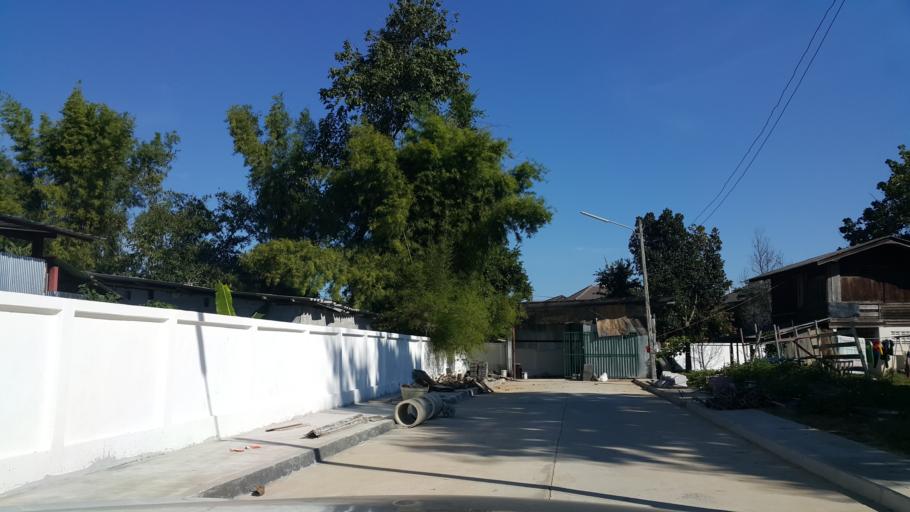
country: TH
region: Chiang Mai
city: San Sai
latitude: 18.8487
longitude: 98.9971
